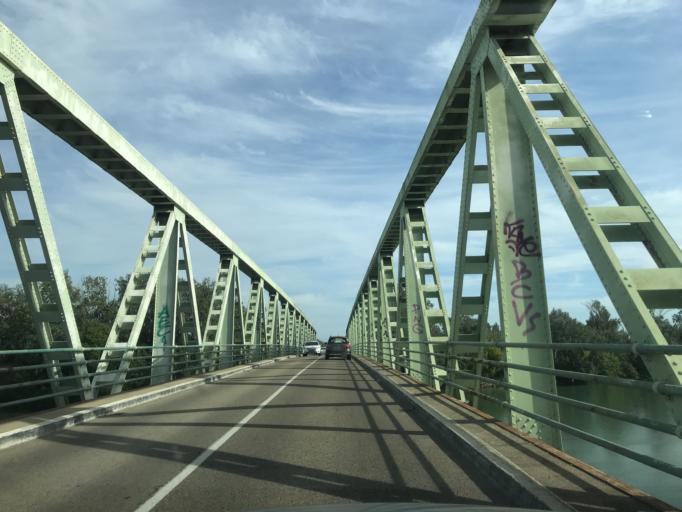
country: FR
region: Provence-Alpes-Cote d'Azur
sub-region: Departement des Bouches-du-Rhone
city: Saintes-Maries-de-la-Mer
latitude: 43.5470
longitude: 4.3494
